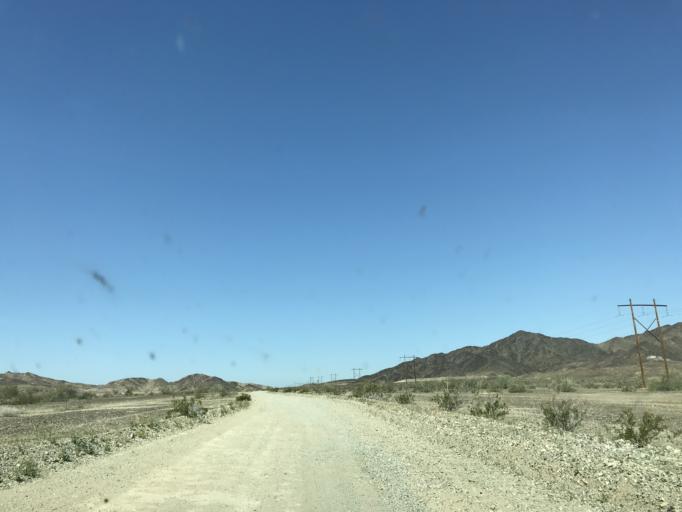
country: US
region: California
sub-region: Riverside County
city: Mesa Verde
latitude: 33.4933
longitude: -114.8151
